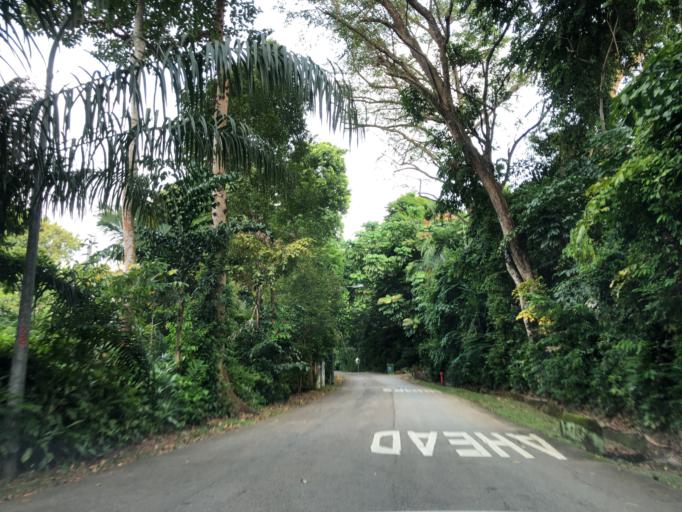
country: SG
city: Singapore
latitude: 1.3134
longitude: 103.8331
